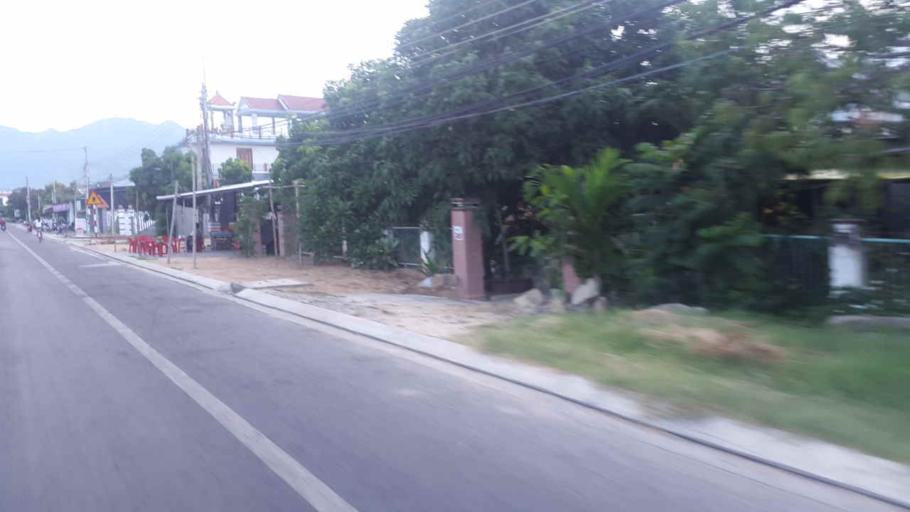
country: VN
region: Khanh Hoa
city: Cam Lam
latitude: 12.0759
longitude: 109.1571
